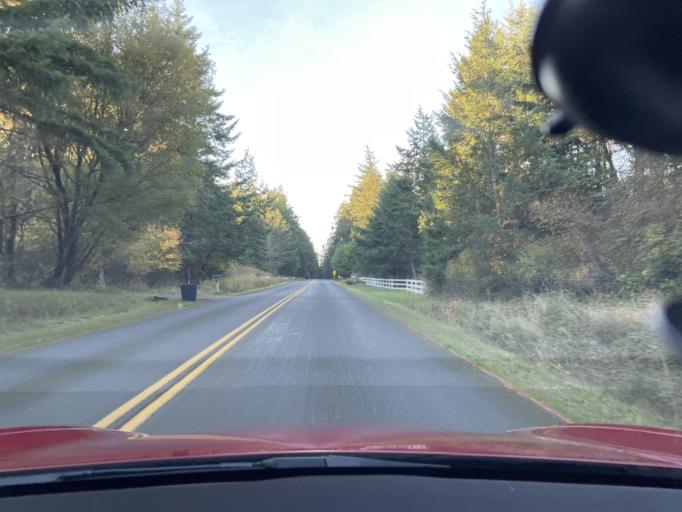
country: US
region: Washington
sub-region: San Juan County
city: Friday Harbor
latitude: 48.5625
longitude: -123.1648
